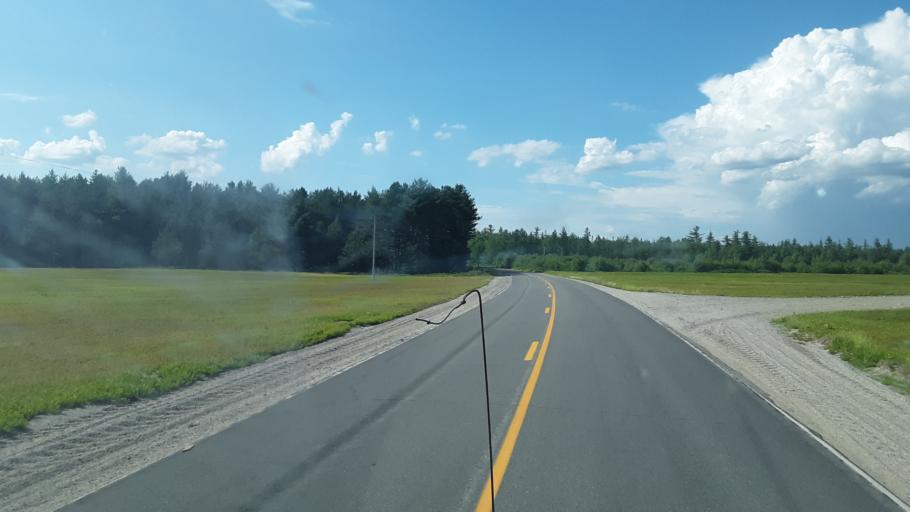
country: US
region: Maine
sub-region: Washington County
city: Cherryfield
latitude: 44.7646
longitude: -68.0272
